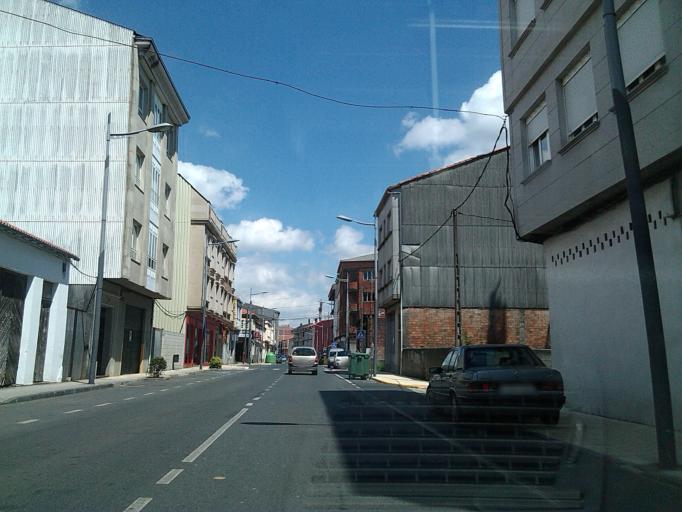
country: ES
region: Galicia
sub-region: Provincia da Coruna
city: Melide
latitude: 42.9168
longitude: -8.0165
